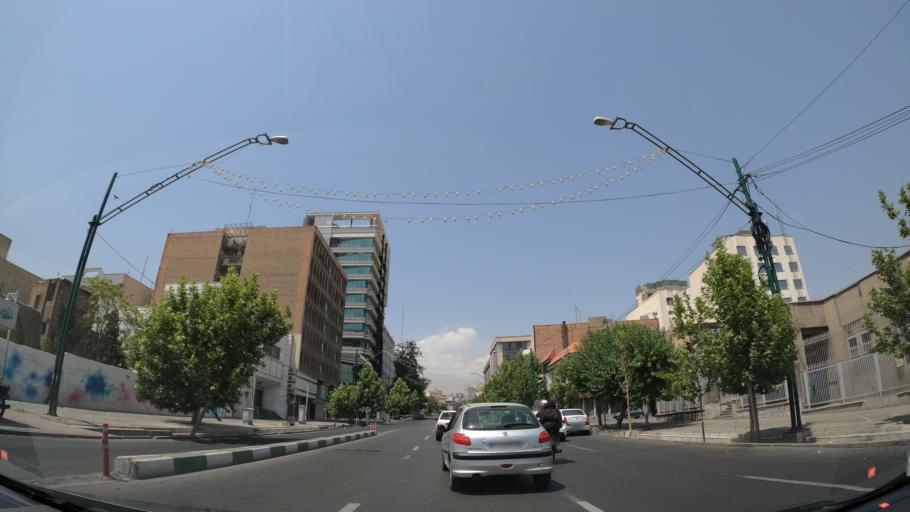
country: IR
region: Tehran
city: Tehran
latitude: 35.7253
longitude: 51.4141
